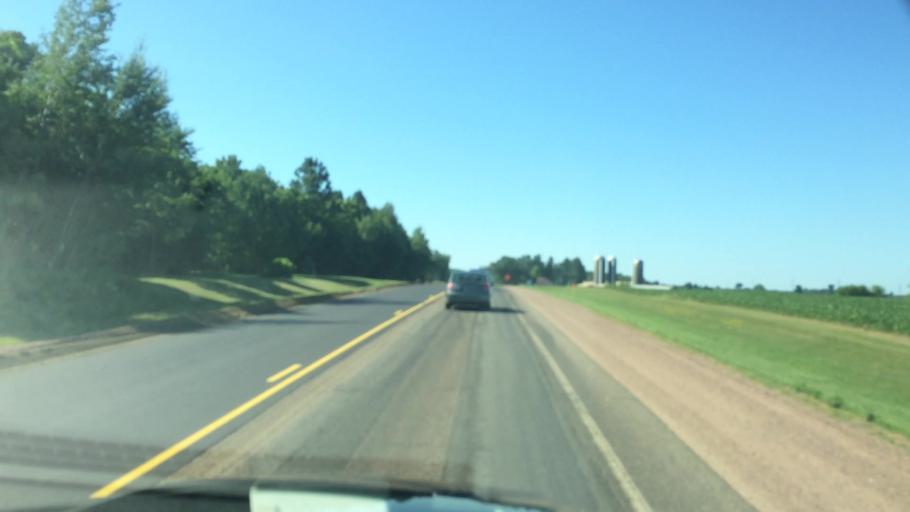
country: US
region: Wisconsin
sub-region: Marathon County
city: Stratford
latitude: 44.8677
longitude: -90.0791
